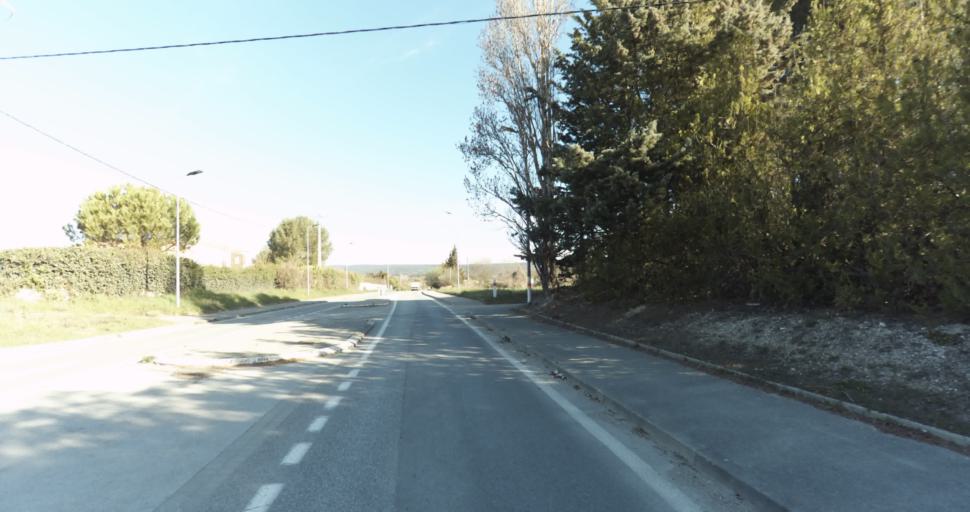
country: FR
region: Provence-Alpes-Cote d'Azur
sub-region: Departement des Bouches-du-Rhone
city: Aix-en-Provence
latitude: 43.5664
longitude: 5.4340
